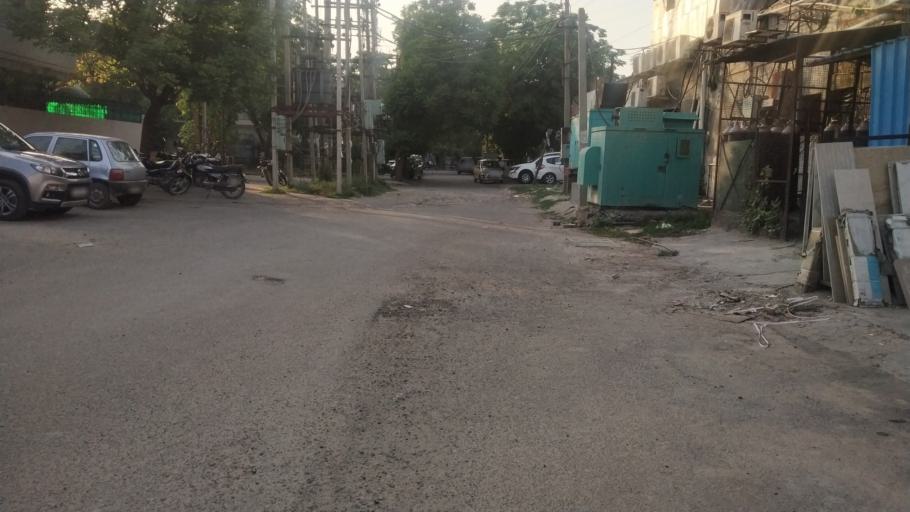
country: IN
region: Punjab
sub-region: Ajitgarh
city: Mohali
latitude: 30.7088
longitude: 76.7224
